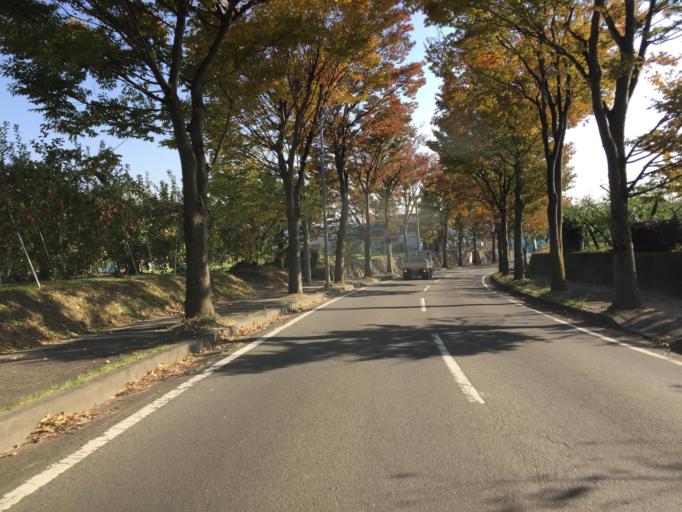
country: JP
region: Fukushima
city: Fukushima-shi
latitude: 37.8307
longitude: 140.4657
